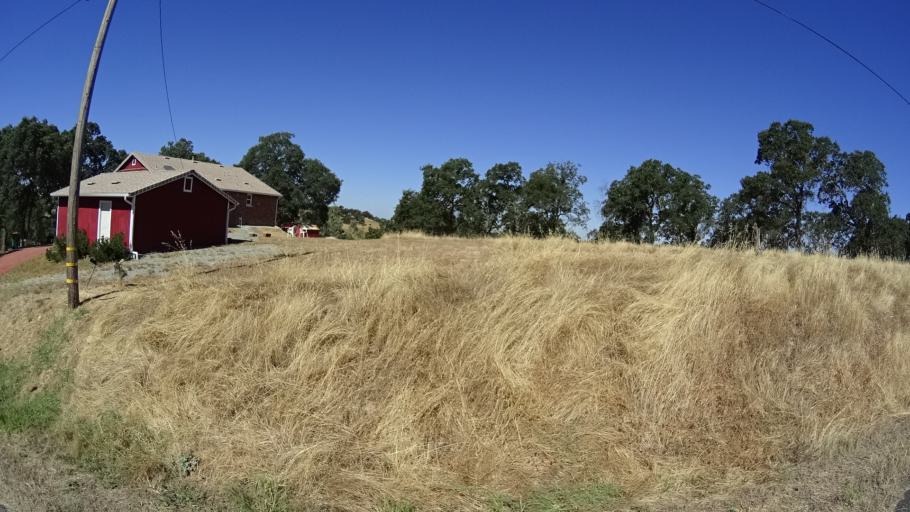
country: US
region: California
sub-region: Calaveras County
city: Rancho Calaveras
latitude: 38.1068
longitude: -120.8758
